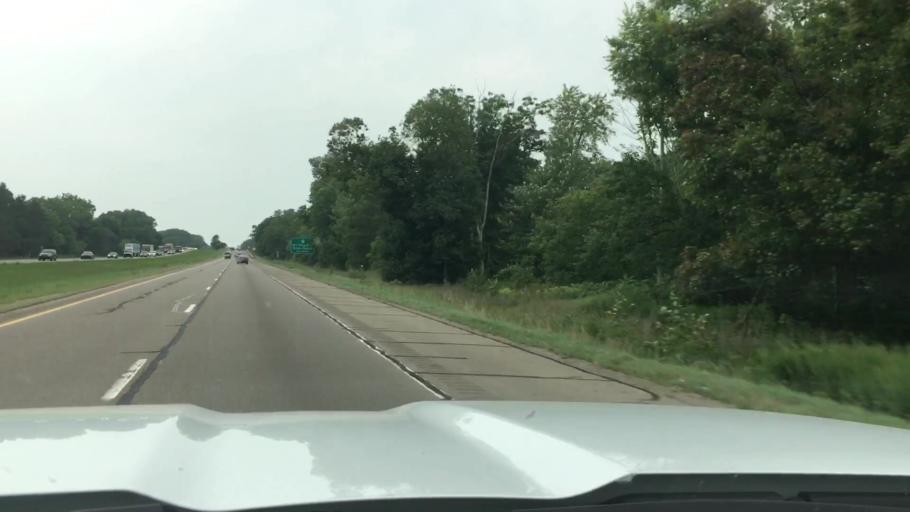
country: US
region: Michigan
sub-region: Ingham County
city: Holt
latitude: 42.6601
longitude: -84.5557
